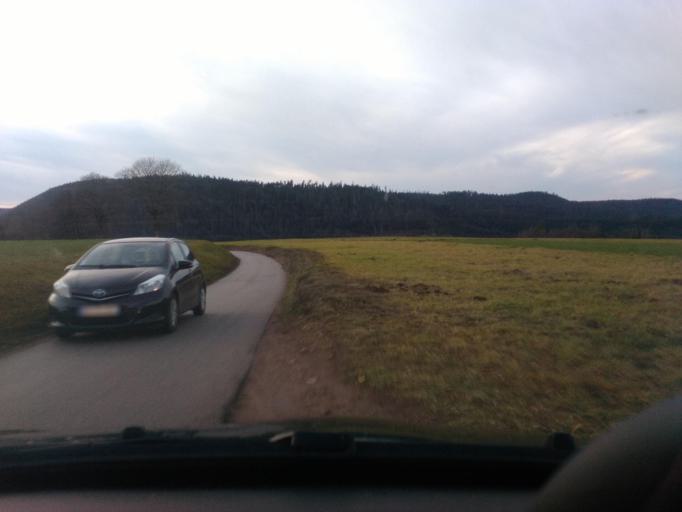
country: FR
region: Lorraine
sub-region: Departement des Vosges
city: Corcieux
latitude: 48.2056
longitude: 6.8971
